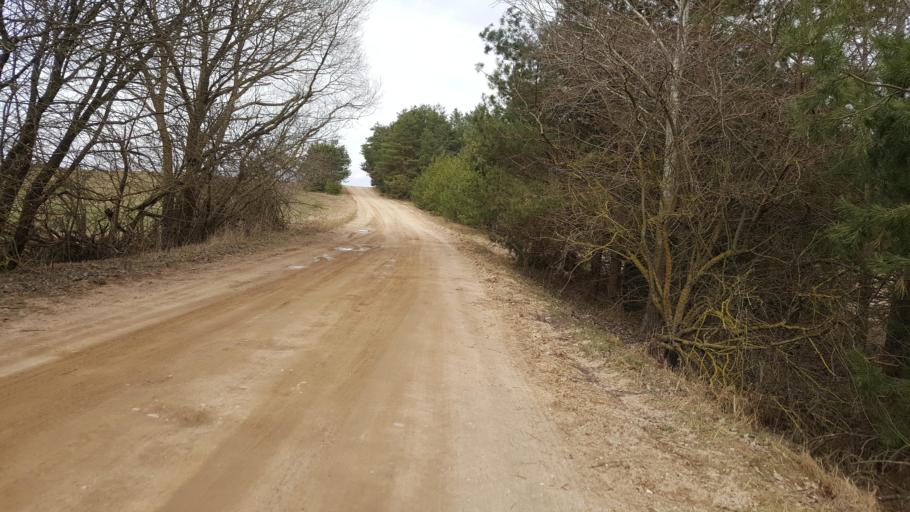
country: BY
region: Brest
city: Kamyanyets
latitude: 52.3678
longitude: 23.9772
